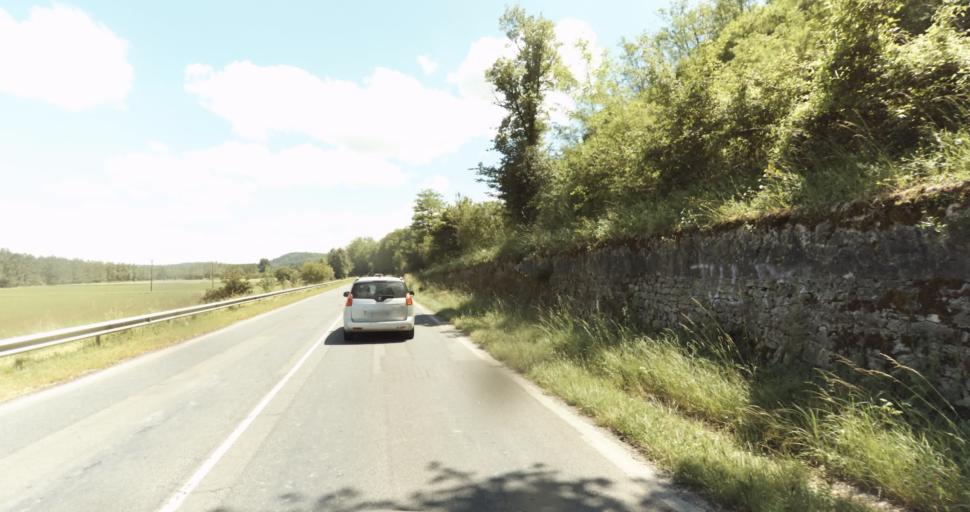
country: FR
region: Aquitaine
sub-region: Departement de la Dordogne
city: Le Bugue
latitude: 44.8390
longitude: 0.9337
